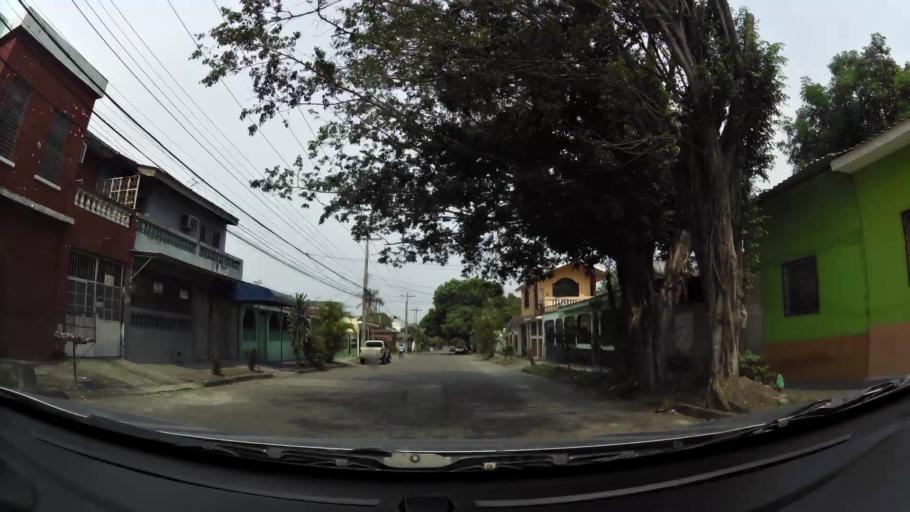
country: HN
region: Cortes
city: San Pedro Sula
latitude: 15.4935
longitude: -88.0310
